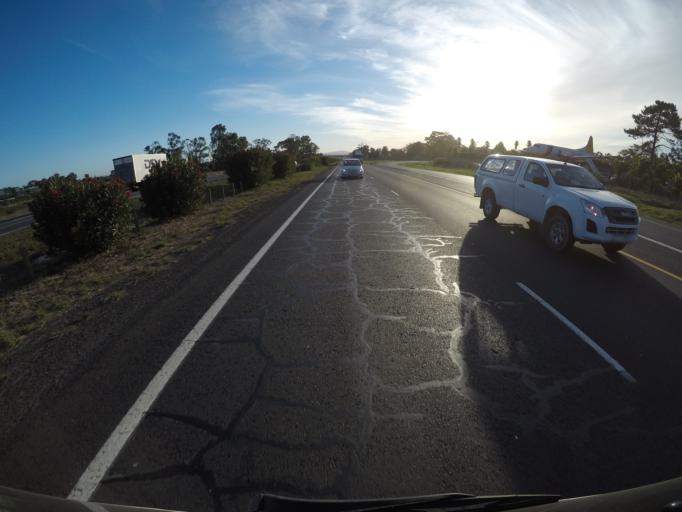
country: ZA
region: Western Cape
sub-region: City of Cape Town
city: Kraaifontein
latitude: -33.8342
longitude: 18.7398
